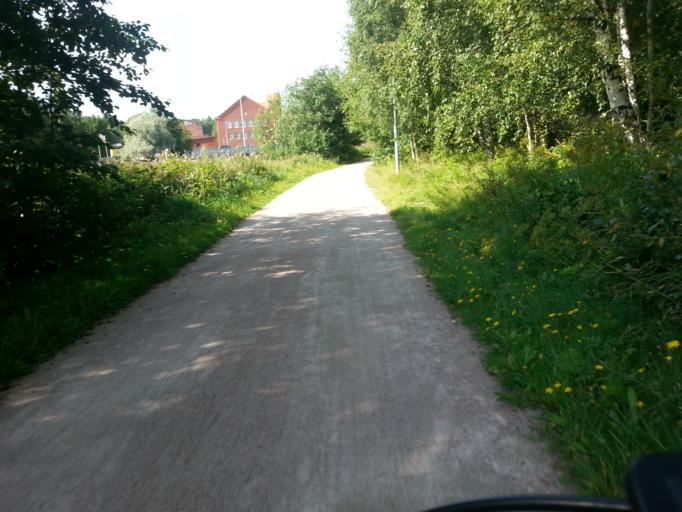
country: FI
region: Uusimaa
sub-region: Helsinki
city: Helsinki
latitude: 60.2182
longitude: 24.9802
